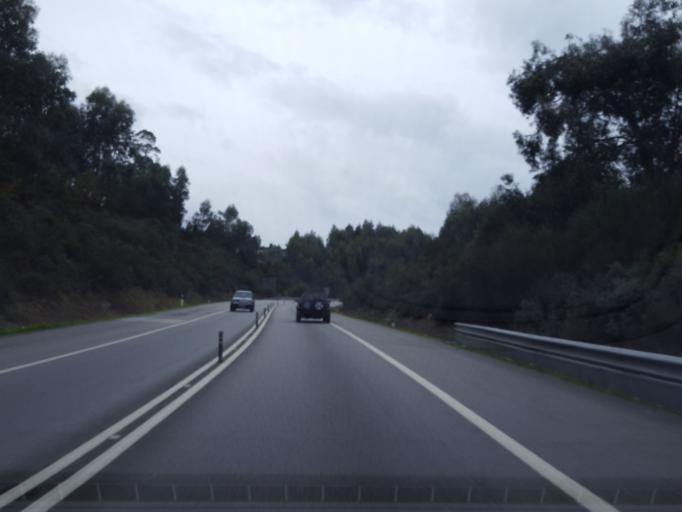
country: PT
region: Porto
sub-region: Marco de Canaveses
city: Marco de Canavezes
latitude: 41.2217
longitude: -8.1878
